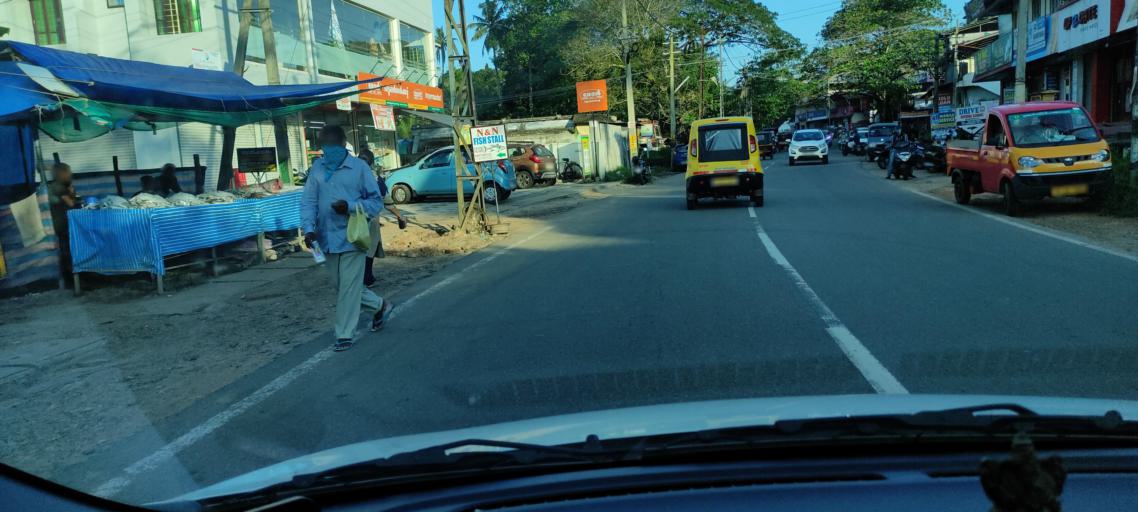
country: IN
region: Kerala
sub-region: Pattanamtitta
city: Adur
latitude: 9.1489
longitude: 76.7578
